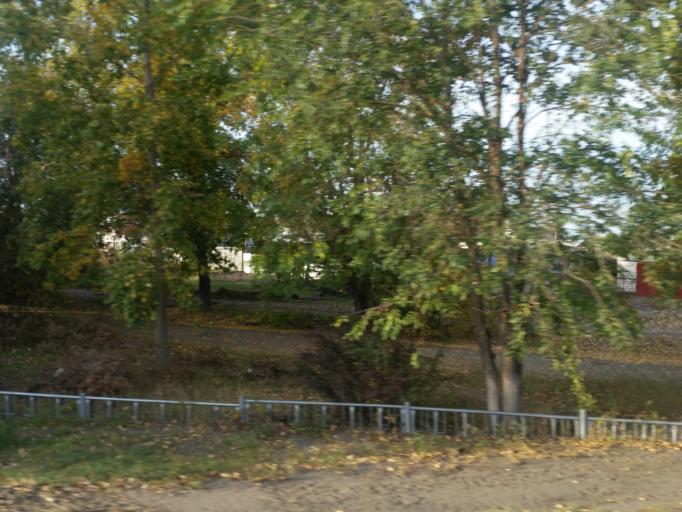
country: RU
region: Ulyanovsk
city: Cherdakly
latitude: 54.3561
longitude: 48.8554
